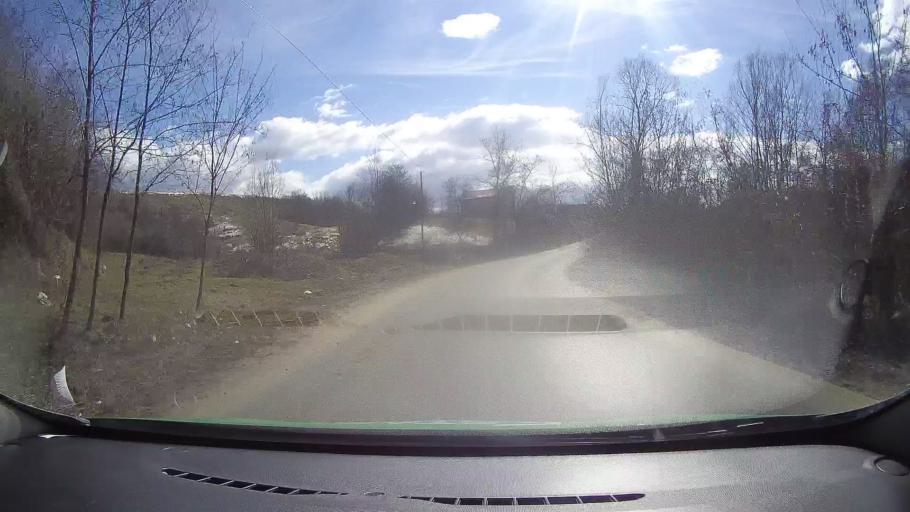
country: RO
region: Dambovita
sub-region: Comuna Vulcana-Pandele
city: Gura Vulcanei
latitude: 45.0392
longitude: 25.3911
